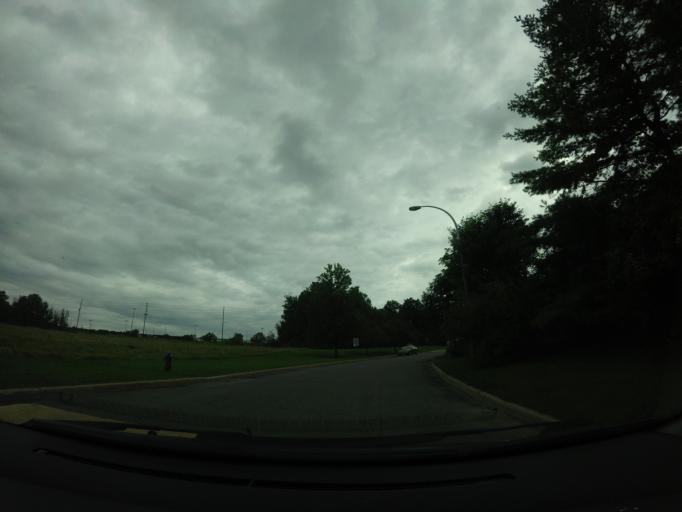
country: CA
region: Quebec
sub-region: Outaouais
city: Gatineau
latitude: 45.4815
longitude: -75.5219
